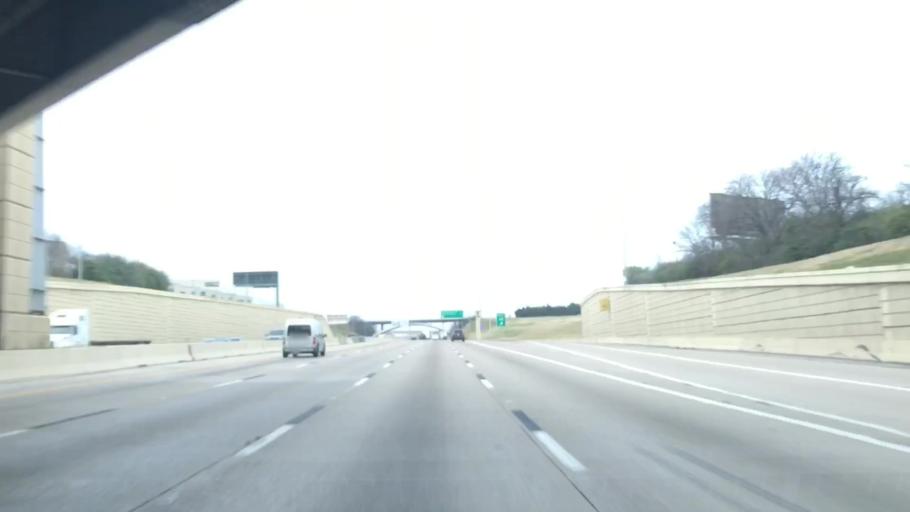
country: US
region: Texas
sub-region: Dallas County
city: Cockrell Hill
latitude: 32.7645
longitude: -96.8501
